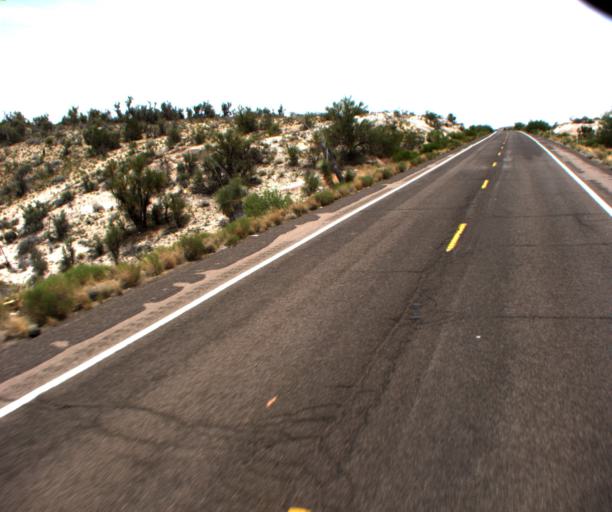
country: US
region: Arizona
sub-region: Graham County
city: Bylas
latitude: 33.2481
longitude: -110.2718
